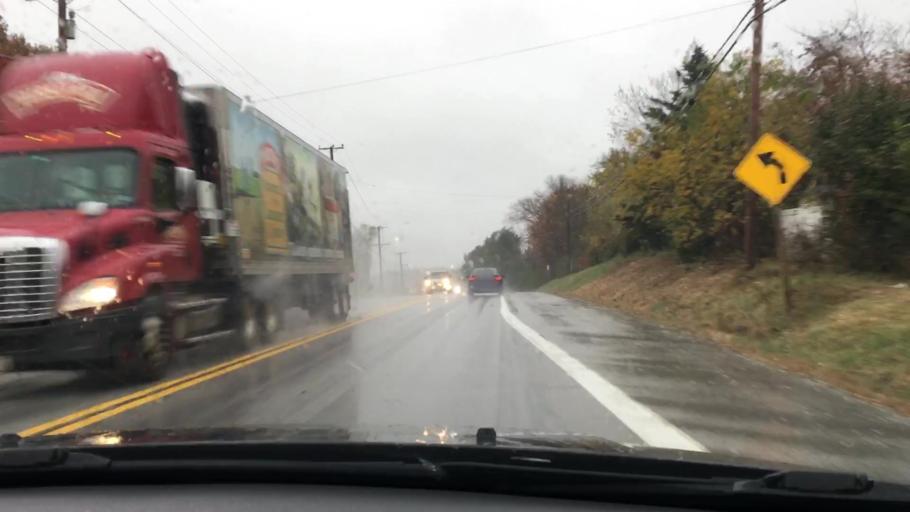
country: US
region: Maryland
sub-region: Carroll County
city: Manchester
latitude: 39.6739
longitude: -76.8918
